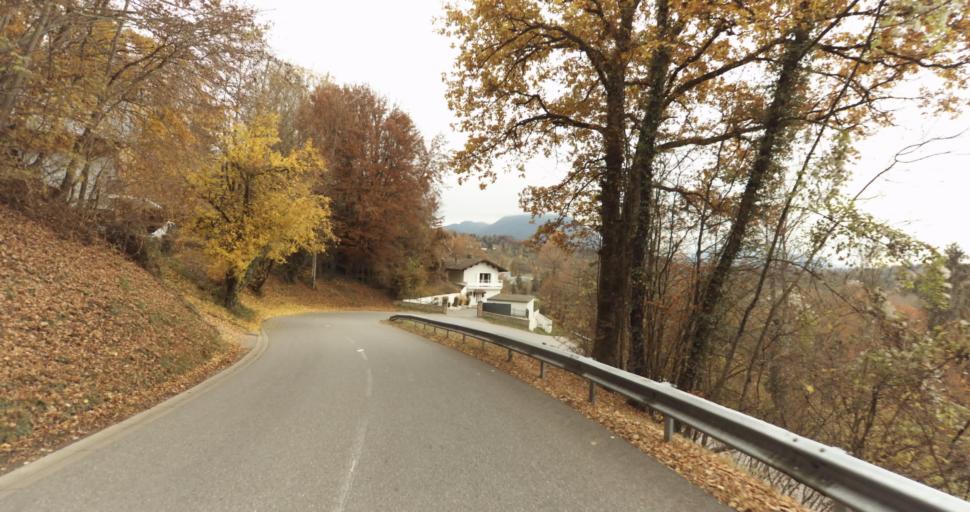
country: FR
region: Rhone-Alpes
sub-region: Departement de la Haute-Savoie
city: Saint-Martin-Bellevue
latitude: 45.9617
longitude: 6.1696
